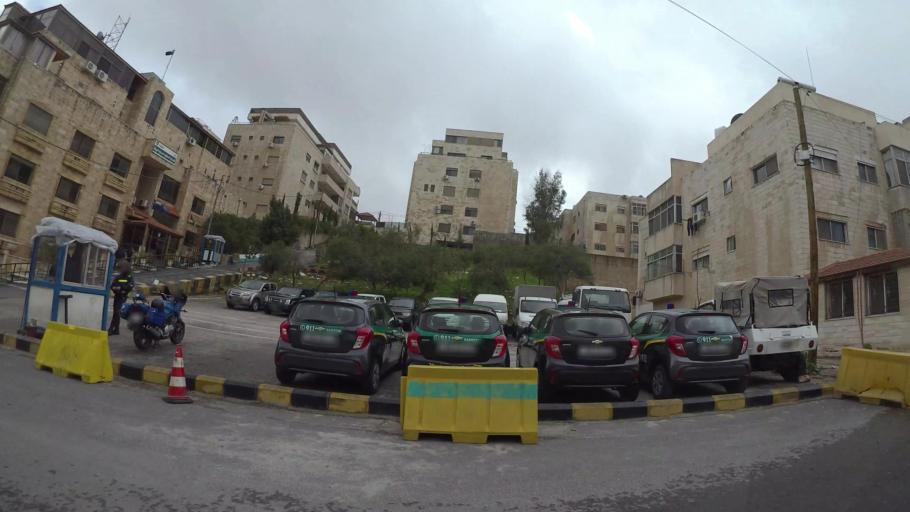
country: JO
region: Amman
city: Al Bunayyat ash Shamaliyah
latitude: 31.9424
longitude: 35.8920
